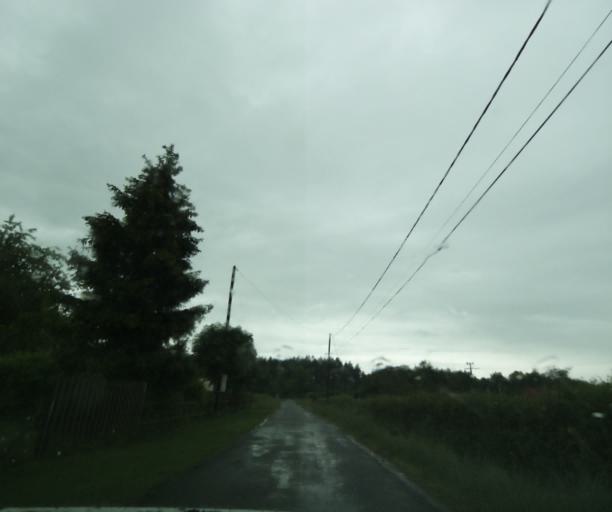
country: FR
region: Bourgogne
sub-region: Departement de Saone-et-Loire
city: Ciry-le-Noble
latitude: 46.5353
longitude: 4.3021
